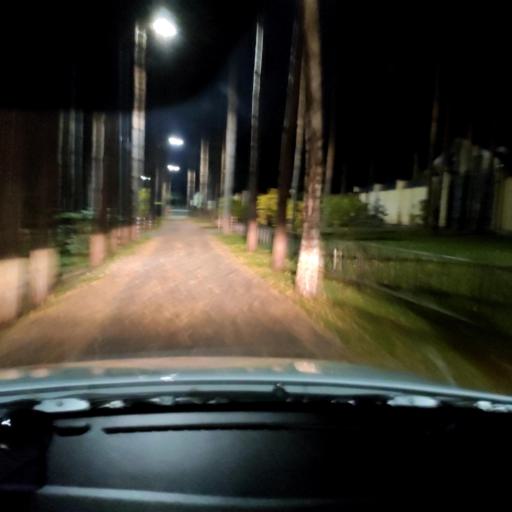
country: RU
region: Tatarstan
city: Verkhniy Uslon
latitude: 55.6221
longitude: 49.0201
